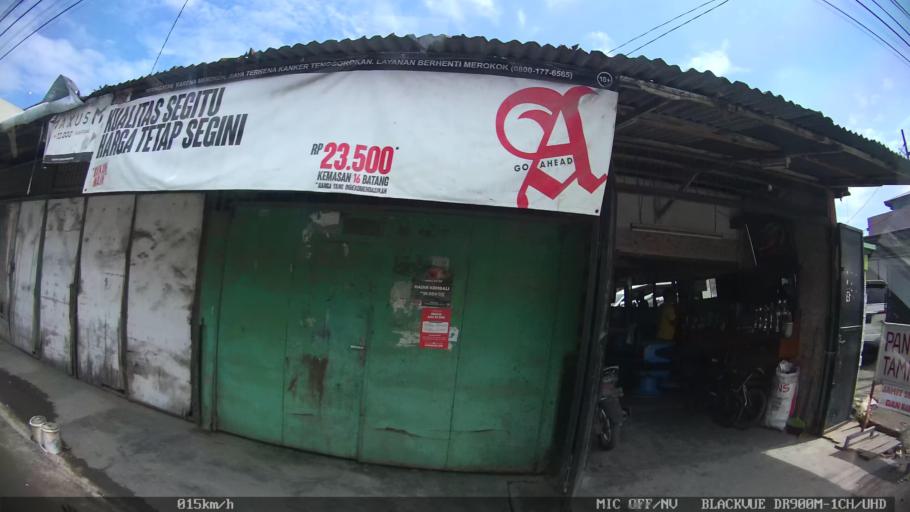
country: ID
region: North Sumatra
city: Medan
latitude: 3.5910
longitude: 98.7543
